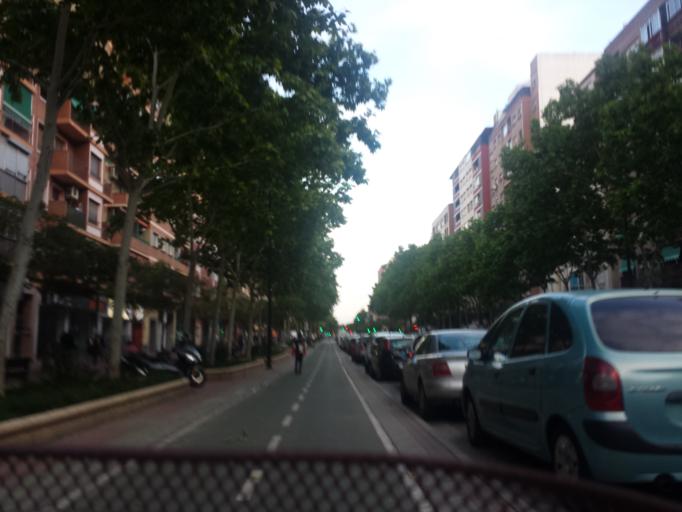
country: ES
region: Aragon
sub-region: Provincia de Zaragoza
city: Delicias
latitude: 41.6520
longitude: -0.9037
